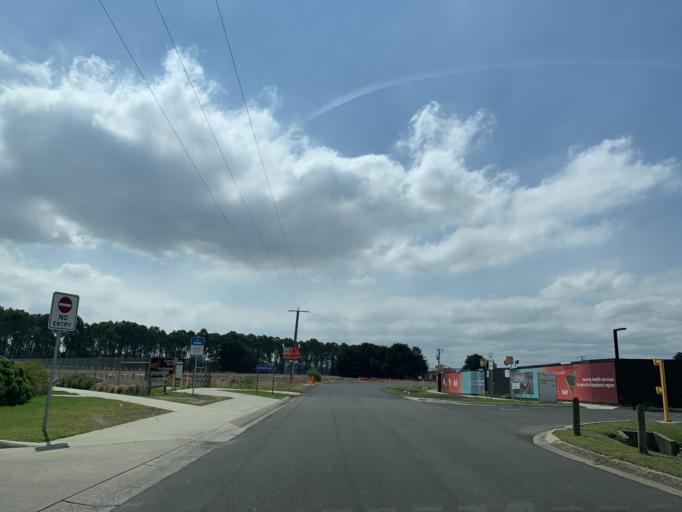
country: AU
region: Victoria
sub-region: Latrobe
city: Traralgon
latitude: -38.2189
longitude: 146.4696
